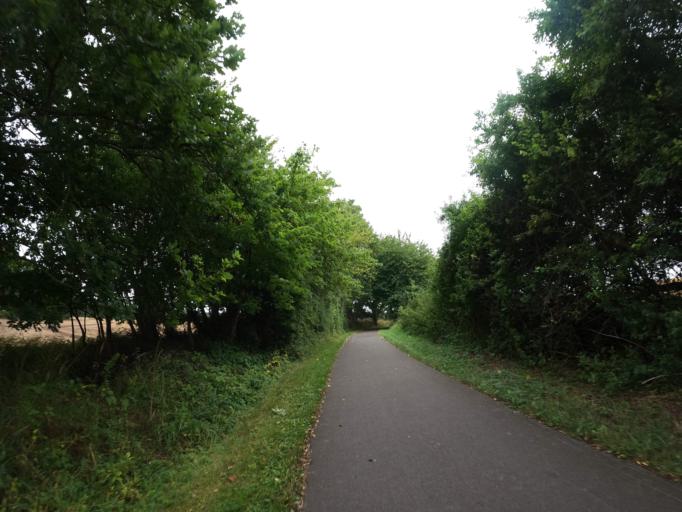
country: DE
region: Mecklenburg-Vorpommern
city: Poseritz
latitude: 54.2916
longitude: 13.2761
